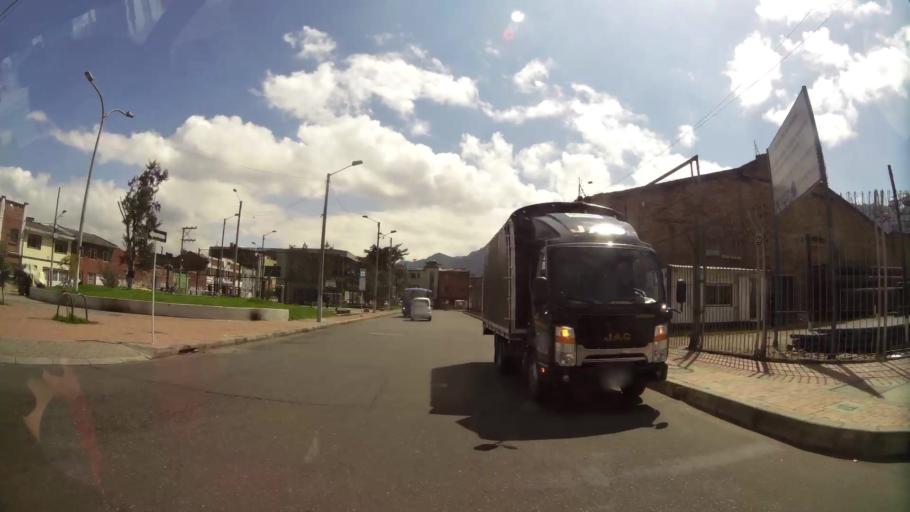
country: CO
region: Bogota D.C.
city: Bogota
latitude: 4.6171
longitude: -74.0800
